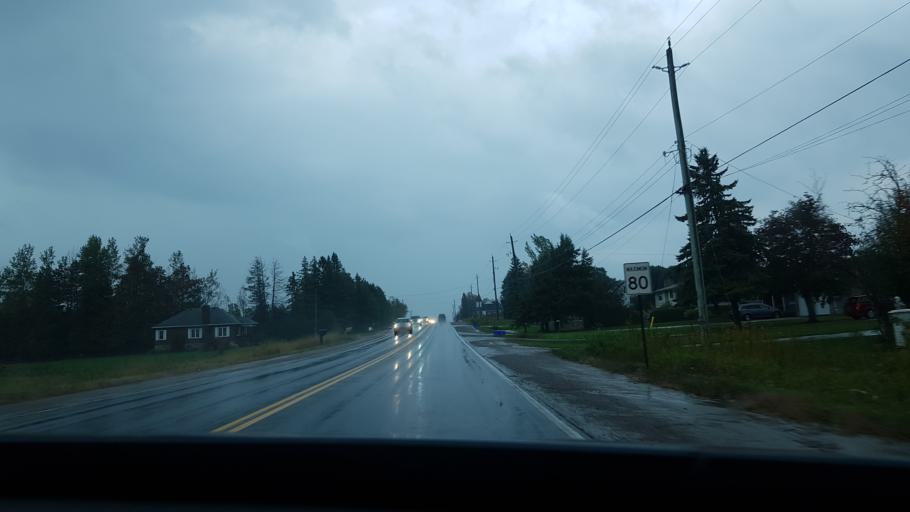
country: CA
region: Ontario
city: Peterborough
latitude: 44.3574
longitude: -78.3703
